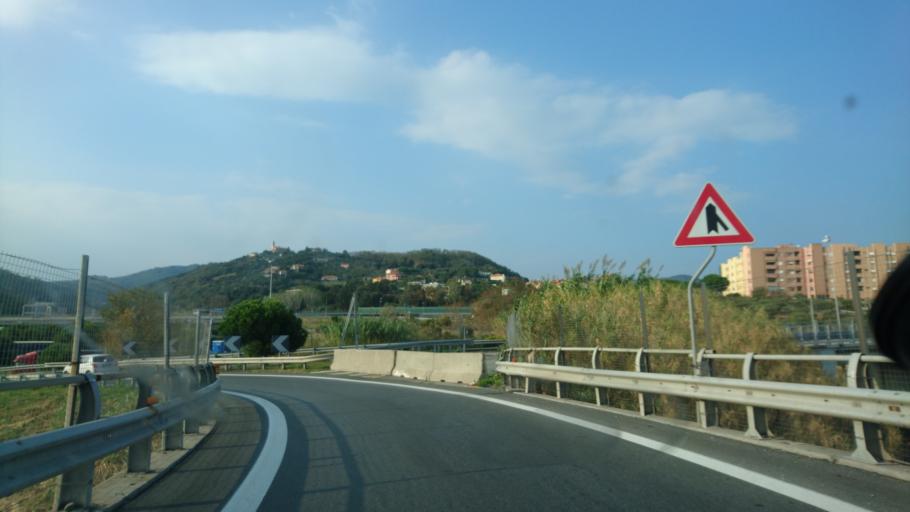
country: IT
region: Liguria
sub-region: Provincia di Savona
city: Valleggia
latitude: 44.2869
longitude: 8.4449
